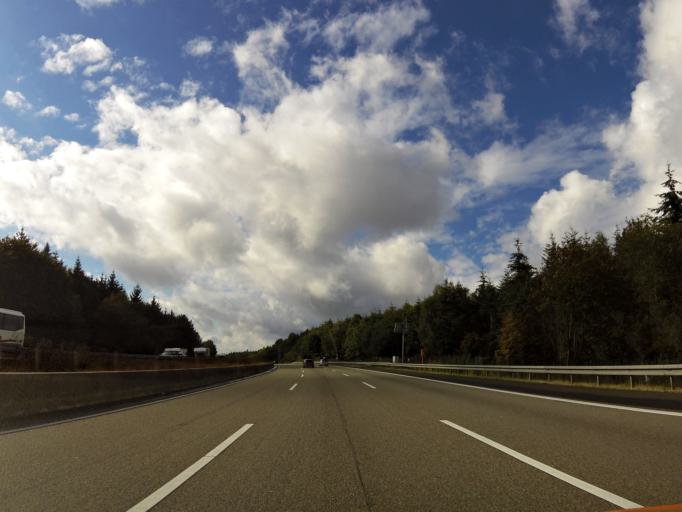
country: DE
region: Hesse
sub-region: Regierungsbezirk Kassel
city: Kirchheim
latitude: 50.8723
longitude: 9.5966
